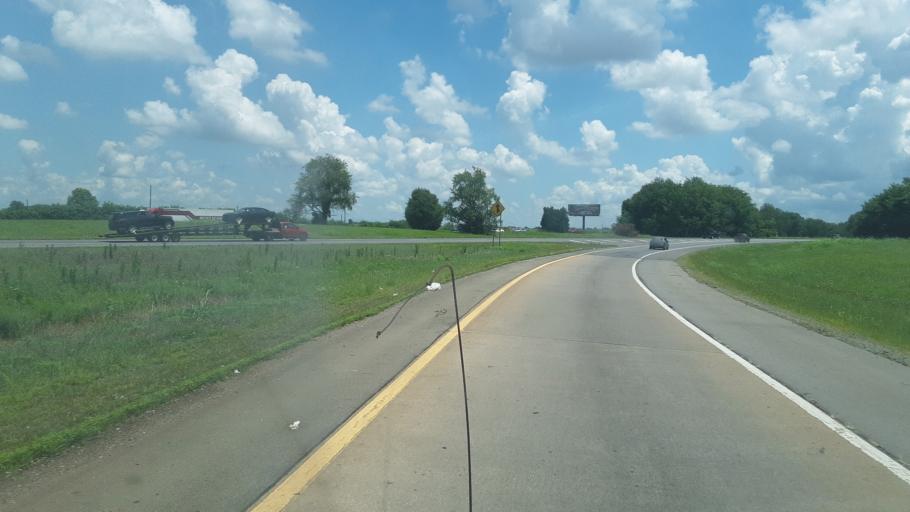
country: US
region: Tennessee
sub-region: Montgomery County
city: Clarksville
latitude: 36.6282
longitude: -87.3147
